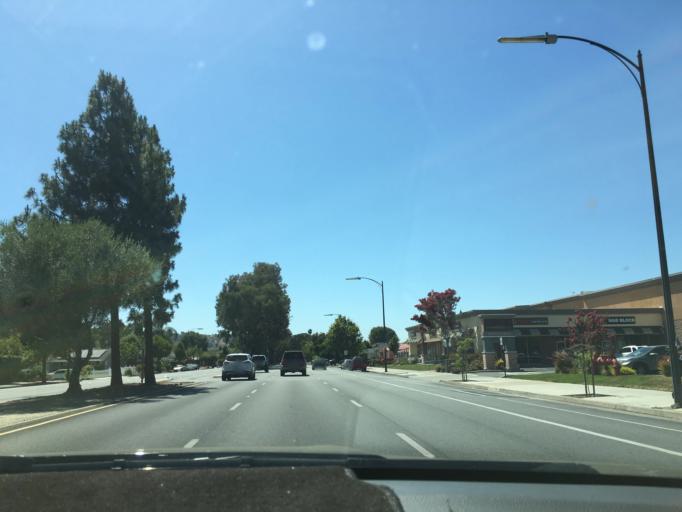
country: US
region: California
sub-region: Santa Clara County
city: Seven Trees
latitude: 37.2370
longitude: -121.8314
